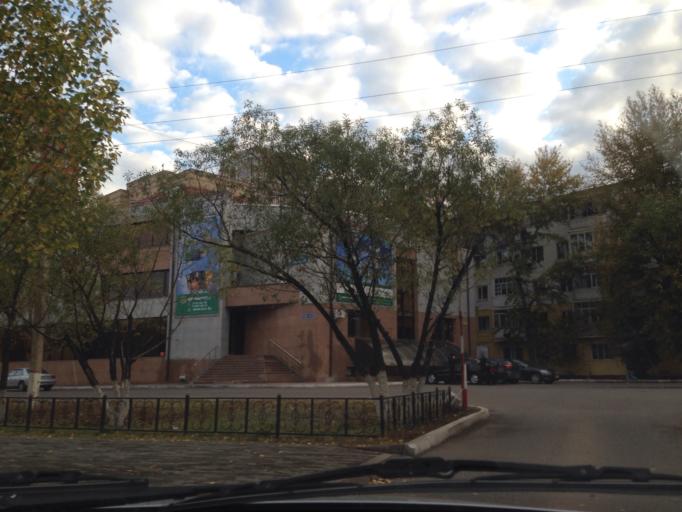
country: KZ
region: Astana Qalasy
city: Astana
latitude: 51.1469
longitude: 71.4596
